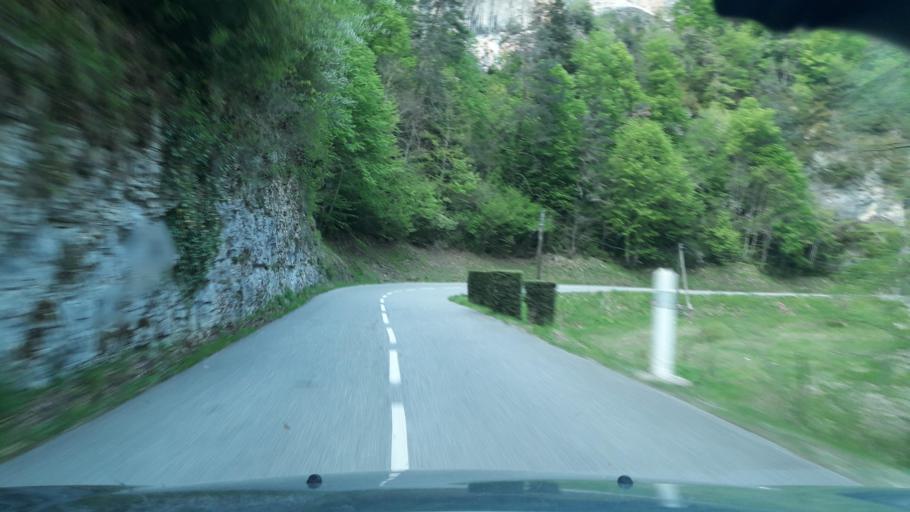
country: FR
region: Rhone-Alpes
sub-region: Departement de la Drome
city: Die
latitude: 44.6778
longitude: 5.5646
